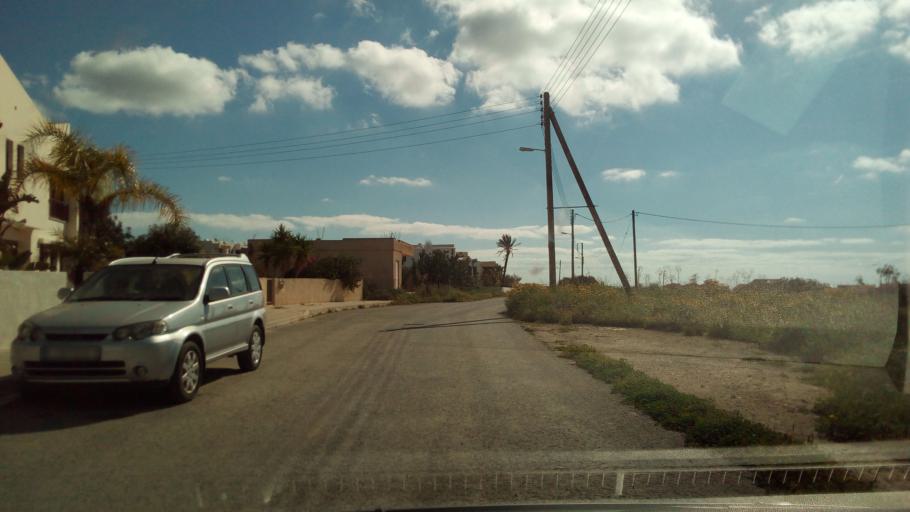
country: CY
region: Larnaka
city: Tersefanou
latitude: 34.8093
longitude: 33.4851
